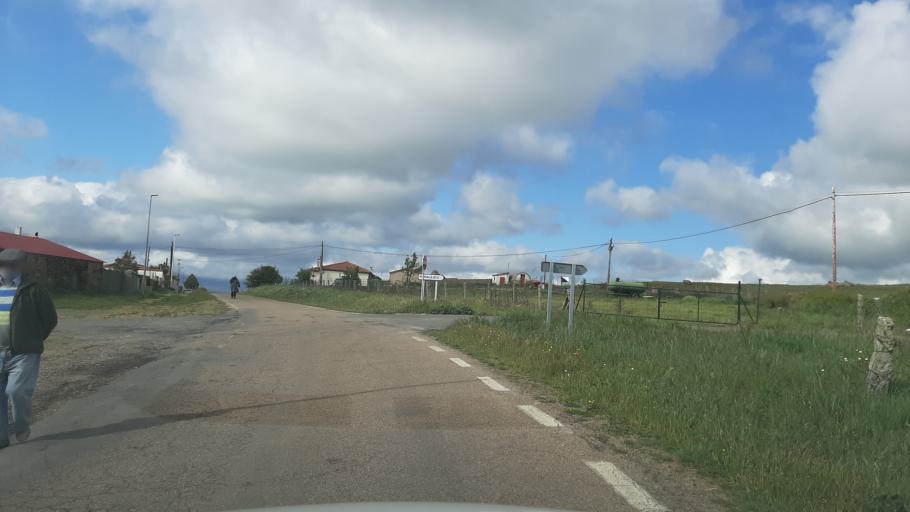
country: ES
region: Castille and Leon
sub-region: Provincia de Salamanca
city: Narros de Matalayegua
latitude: 40.7000
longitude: -5.9279
